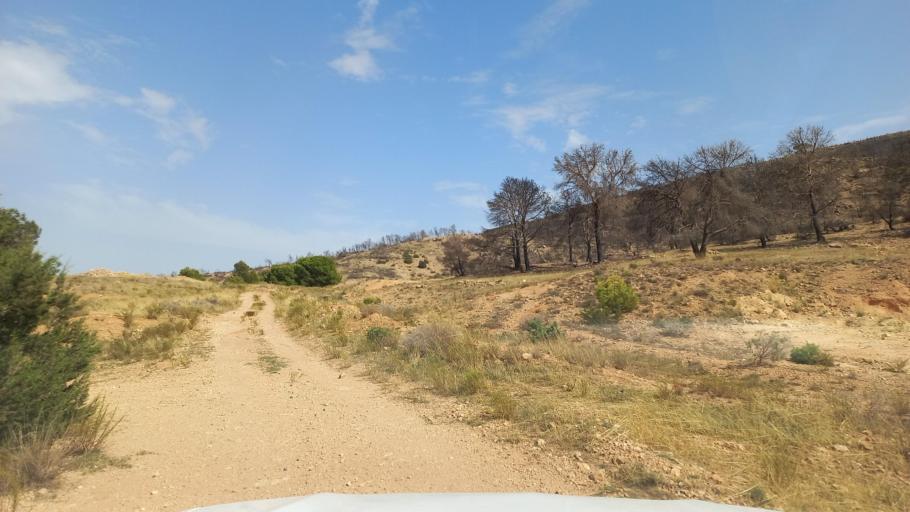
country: TN
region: Al Qasrayn
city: Kasserine
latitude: 35.3531
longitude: 8.8949
